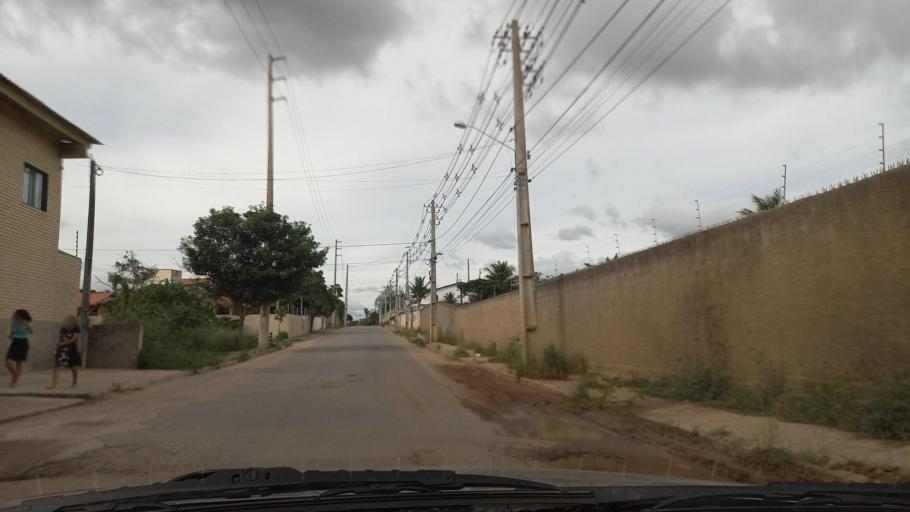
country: BR
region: Pernambuco
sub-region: Gravata
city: Gravata
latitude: -8.2007
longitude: -35.5454
